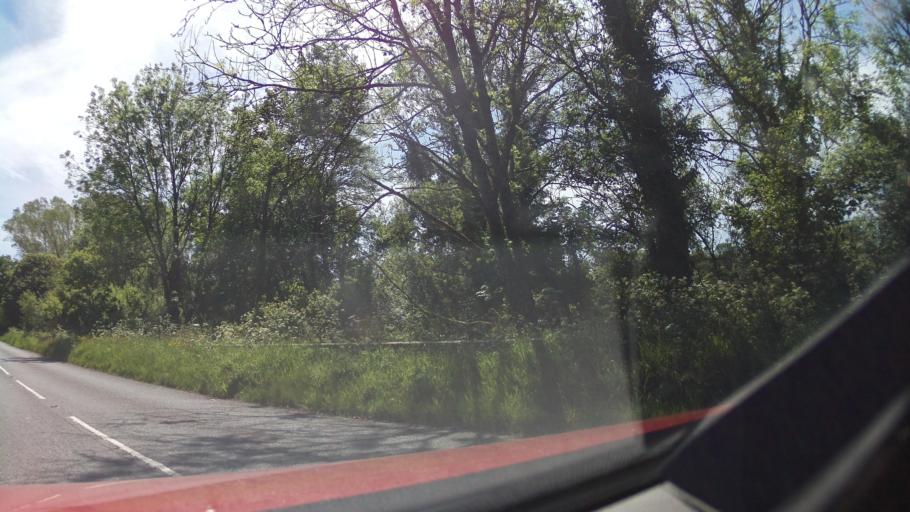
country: GB
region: England
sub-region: Devon
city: Honiton
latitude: 50.8035
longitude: -3.2025
